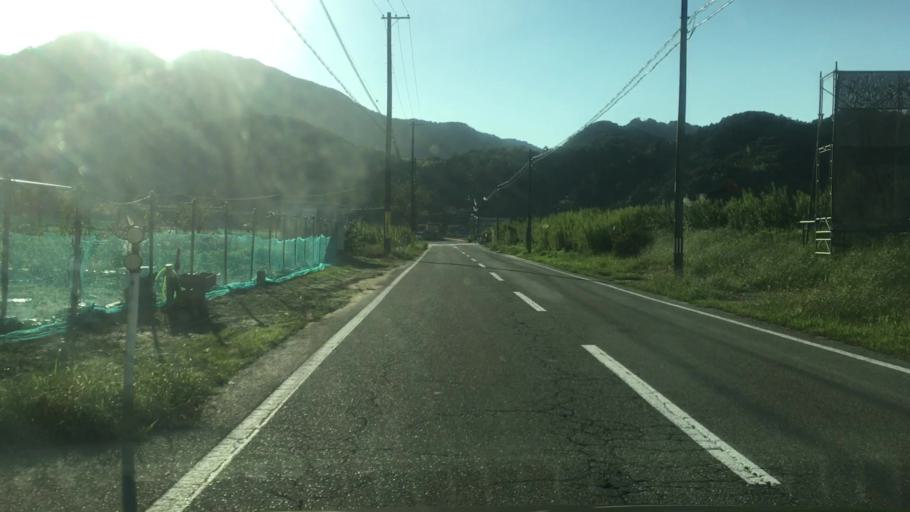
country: JP
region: Hyogo
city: Toyooka
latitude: 35.6191
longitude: 134.8173
